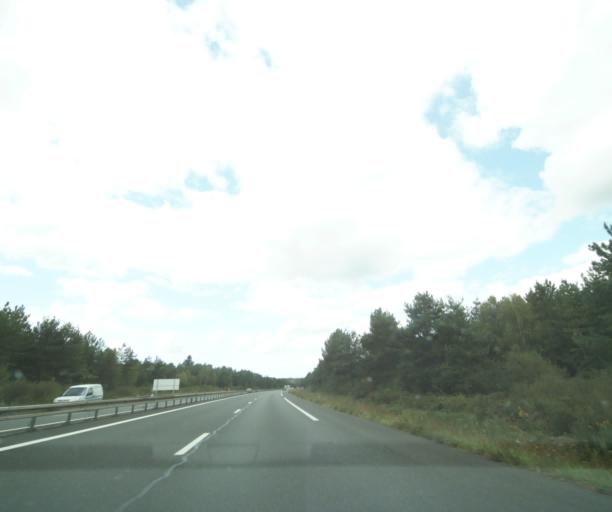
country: FR
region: Centre
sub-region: Departement du Loiret
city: La Ferte-Saint-Aubin
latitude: 47.6816
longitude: 1.9068
